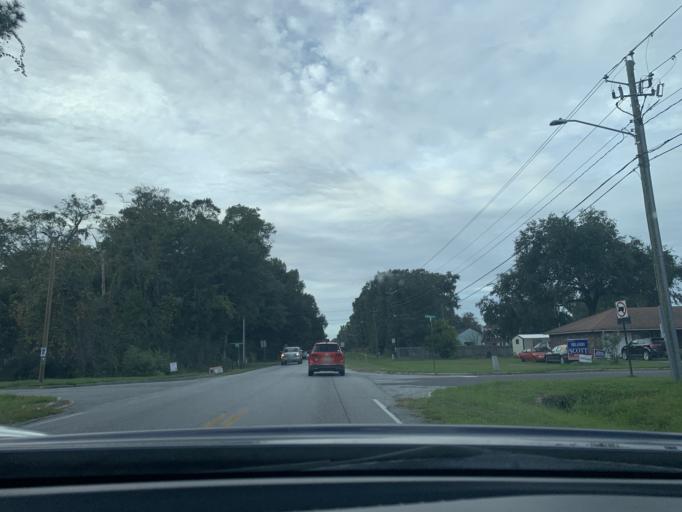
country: US
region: Georgia
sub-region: Chatham County
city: Georgetown
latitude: 32.0251
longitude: -81.2449
